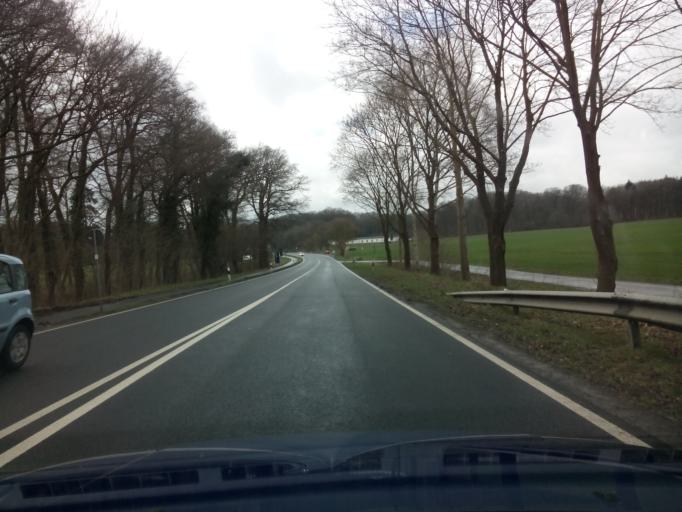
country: DE
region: Lower Saxony
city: Delmenhorst
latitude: 53.0366
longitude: 8.5870
